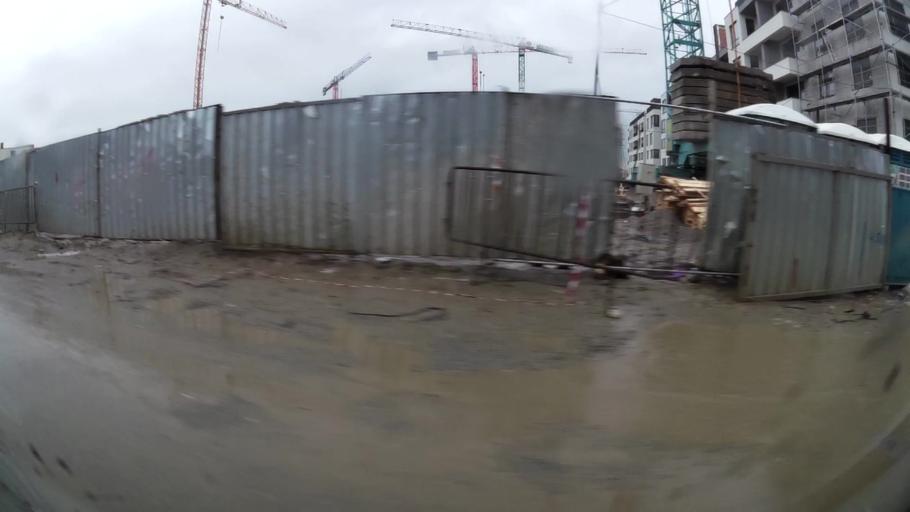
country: BG
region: Sofia-Capital
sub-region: Stolichna Obshtina
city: Sofia
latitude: 42.6546
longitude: 23.3195
